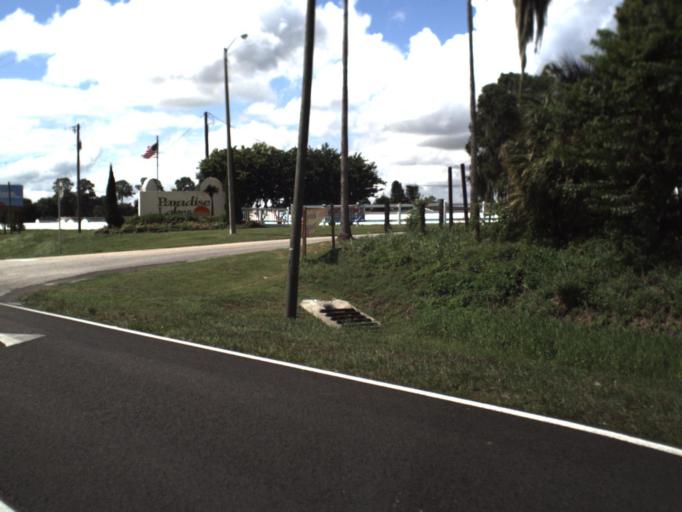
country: US
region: Florida
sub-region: Polk County
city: Mulberry
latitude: 27.9210
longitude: -81.9741
